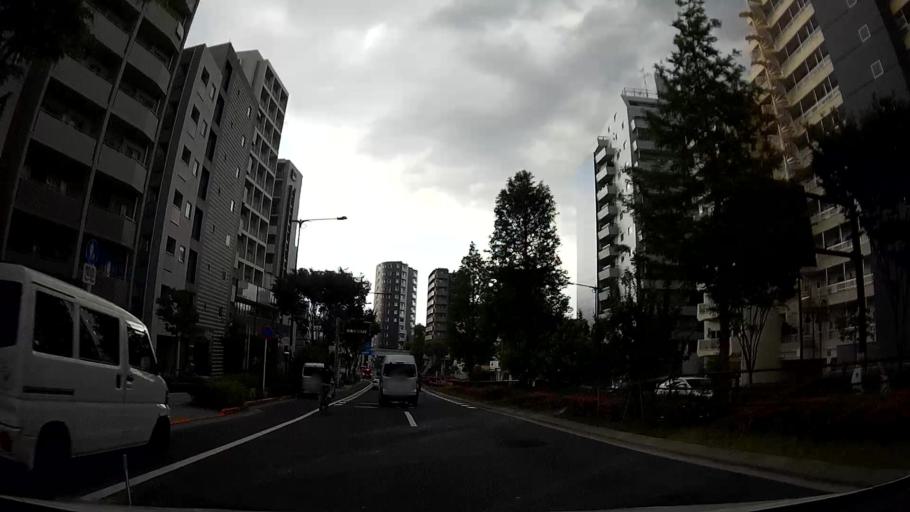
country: JP
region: Tokyo
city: Tokyo
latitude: 35.6994
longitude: 139.6830
